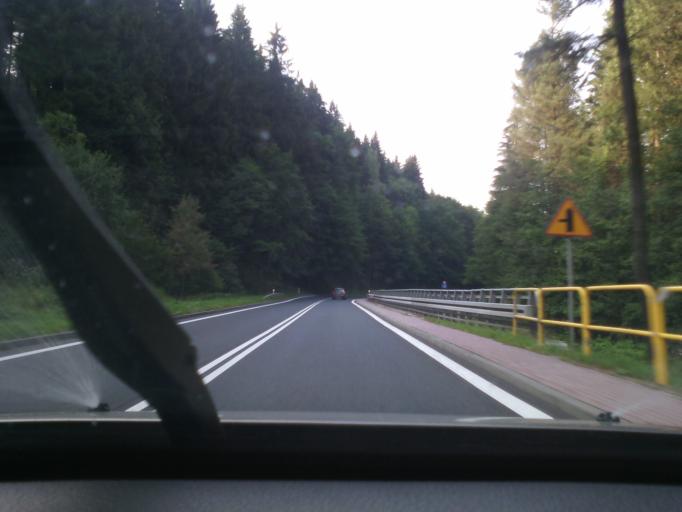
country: PL
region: Lower Silesian Voivodeship
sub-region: Powiat jeleniogorski
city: Piechowice
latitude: 50.8396
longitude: 15.5672
